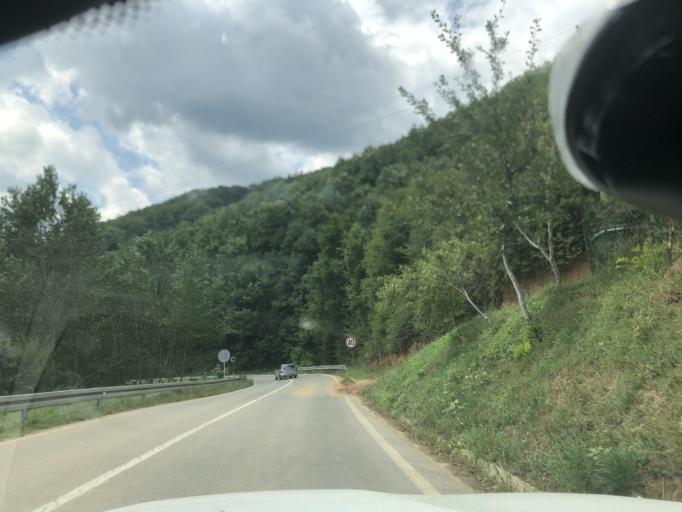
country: RS
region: Central Serbia
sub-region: Jablanicki Okrug
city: Medvega
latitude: 42.8175
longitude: 21.5826
